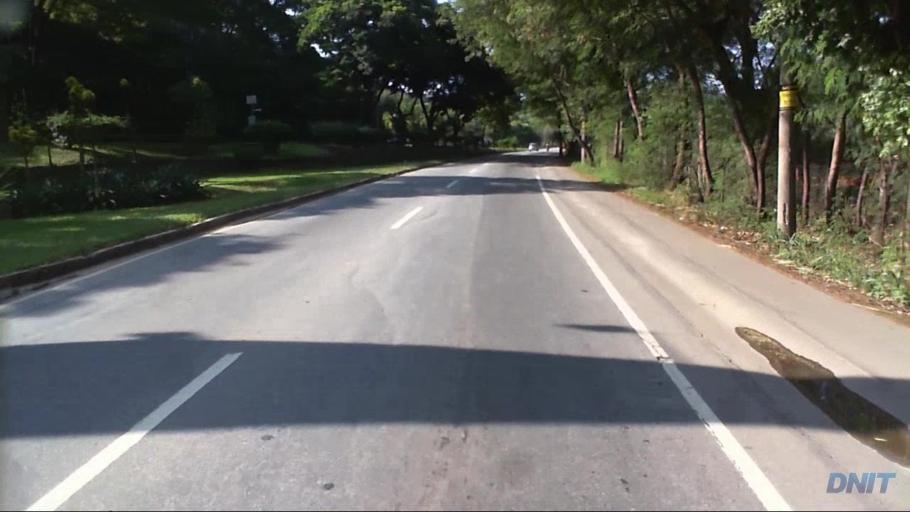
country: BR
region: Minas Gerais
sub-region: Ipatinga
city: Ipatinga
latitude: -19.4909
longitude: -42.5620
